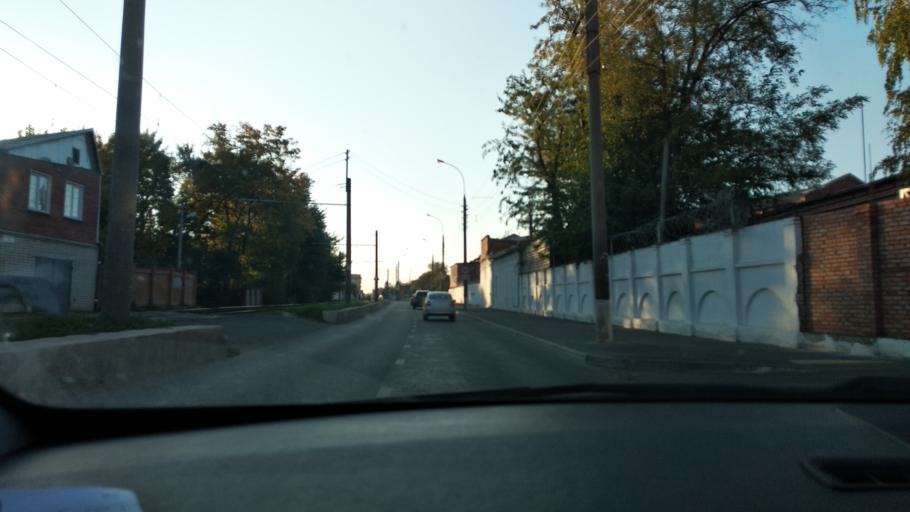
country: RU
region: Krasnodarskiy
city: Krasnodar
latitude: 45.0079
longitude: 39.0154
